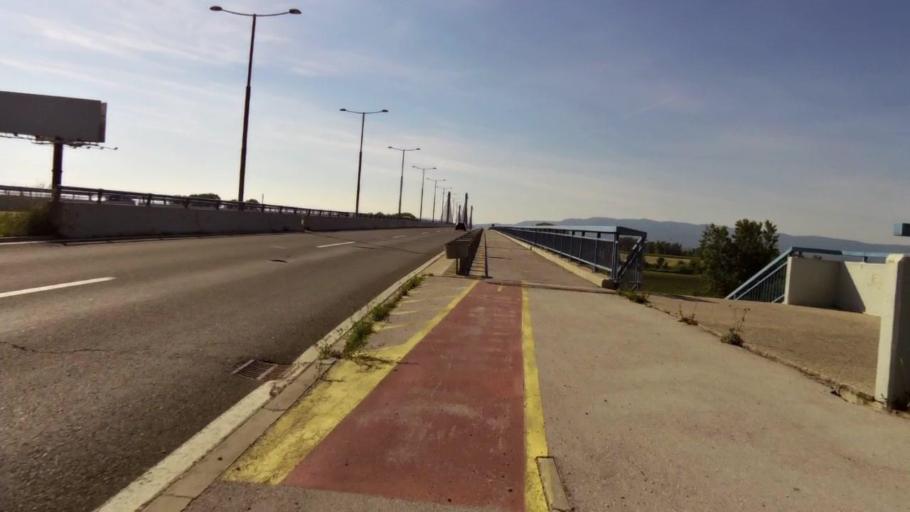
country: HR
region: Zagrebacka
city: Micevec
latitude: 45.7686
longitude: 16.0732
